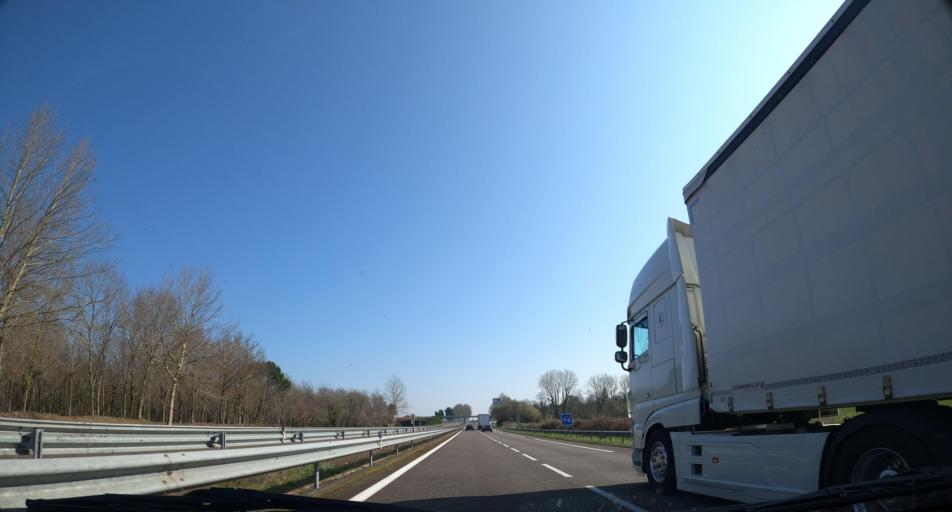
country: FR
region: Aquitaine
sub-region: Departement des Landes
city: Meilhan
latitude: 43.8645
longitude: -0.6715
